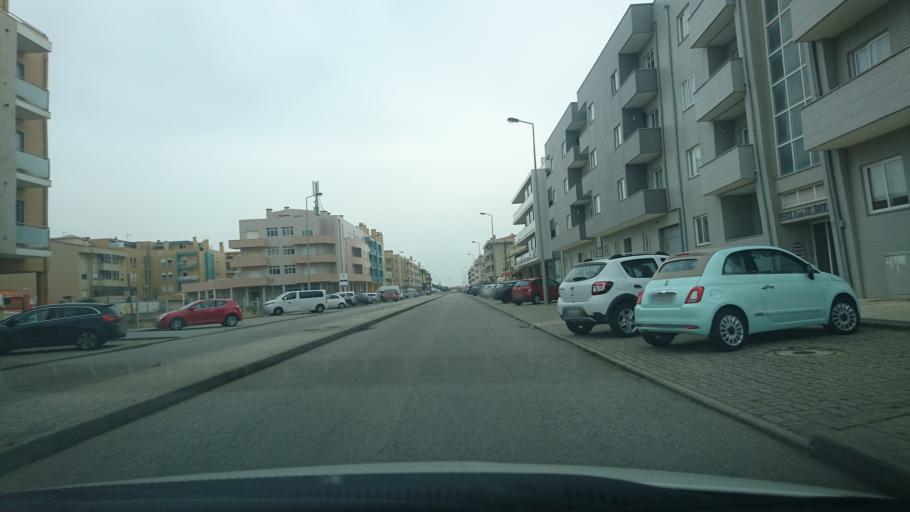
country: PT
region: Aveiro
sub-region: Ovar
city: Esmoriz
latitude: 40.9546
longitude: -8.6531
